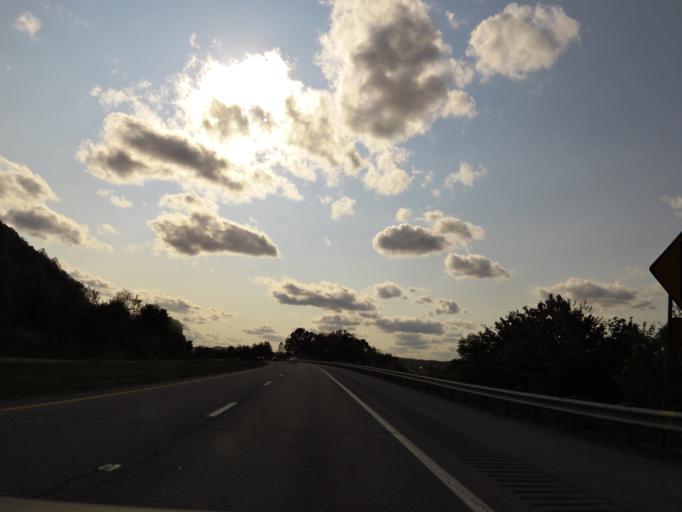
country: US
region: West Virginia
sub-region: Mercer County
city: Princeton
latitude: 37.3625
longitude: -81.0692
